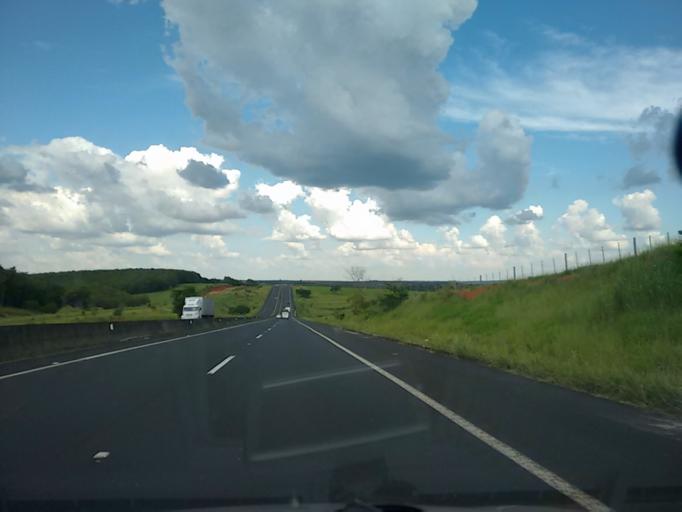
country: BR
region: Sao Paulo
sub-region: Garca
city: Garca
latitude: -22.2265
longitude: -49.7949
